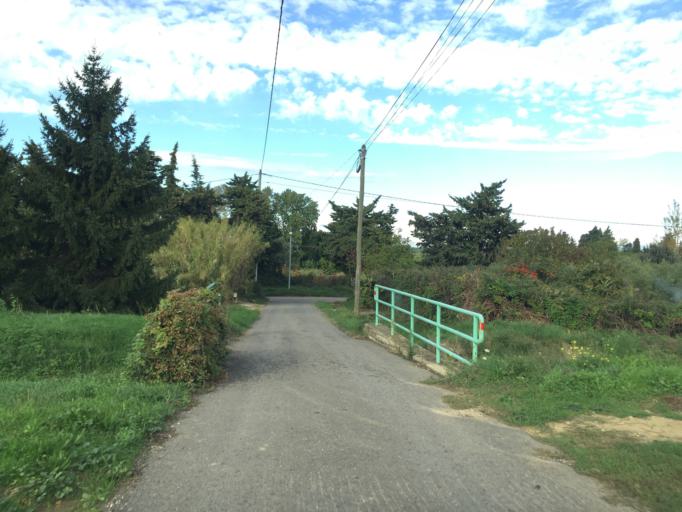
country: FR
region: Provence-Alpes-Cote d'Azur
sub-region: Departement du Vaucluse
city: Orange
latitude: 44.0954
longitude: 4.8088
